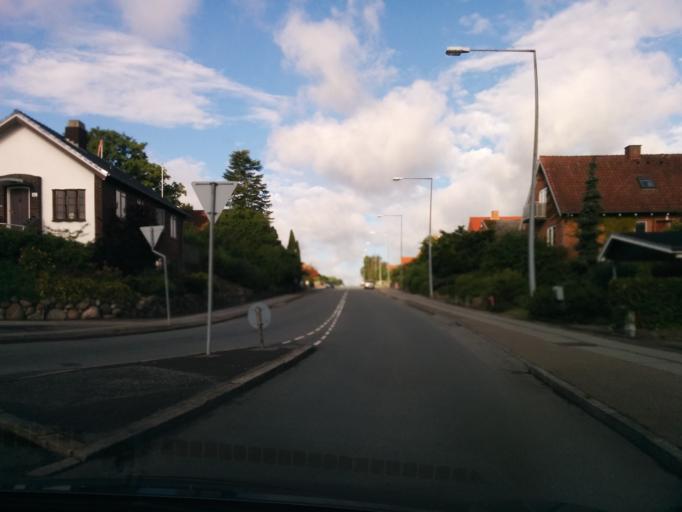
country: DK
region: Central Jutland
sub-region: Arhus Kommune
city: Arhus
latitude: 56.1327
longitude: 10.1895
